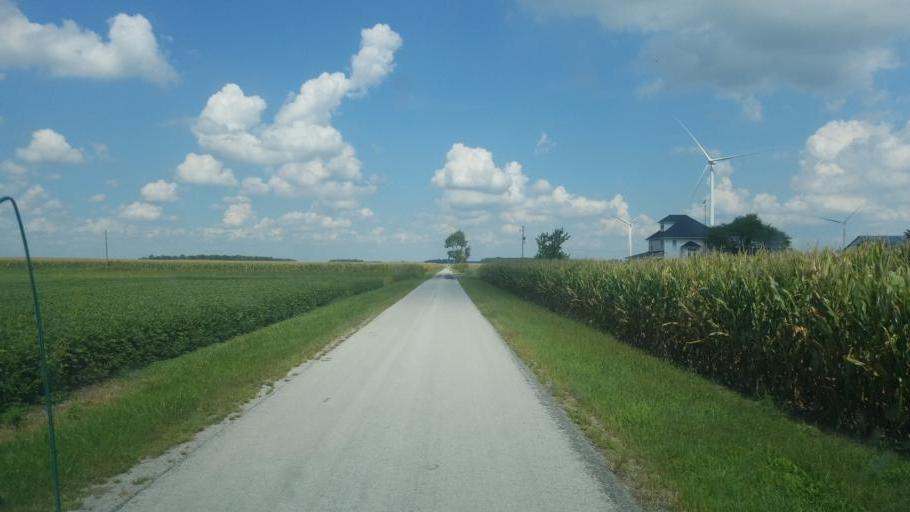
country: US
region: Ohio
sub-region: Hardin County
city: Ada
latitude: 40.7822
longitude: -83.7479
